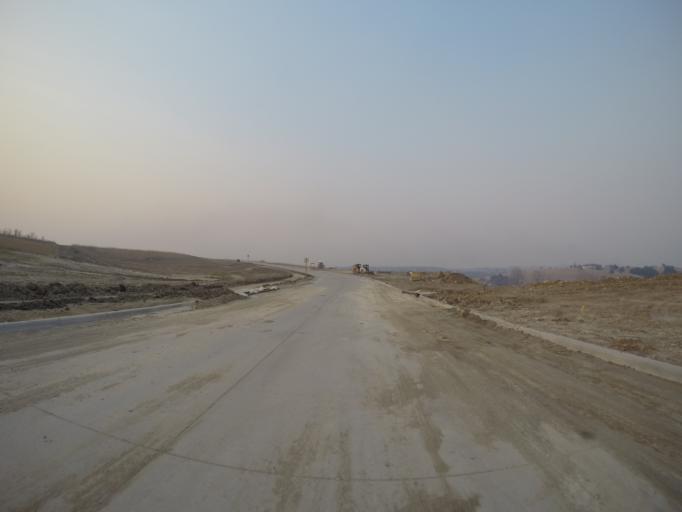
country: US
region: Kansas
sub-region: Riley County
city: Manhattan
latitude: 39.2178
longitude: -96.6384
